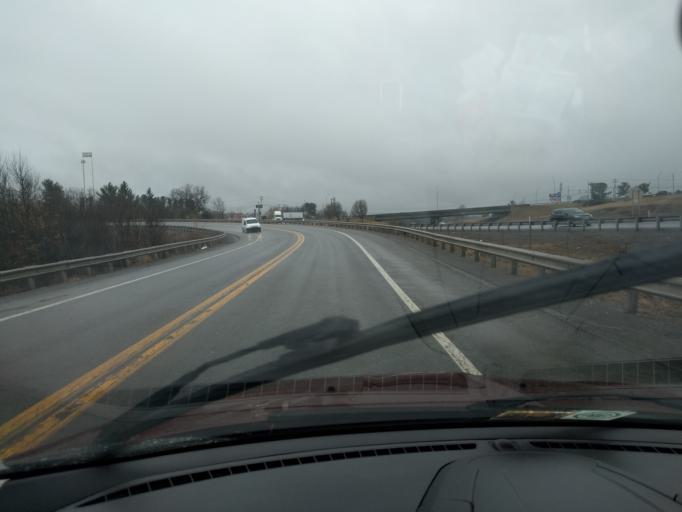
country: US
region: West Virginia
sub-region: Raleigh County
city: Mabscott
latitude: 37.7947
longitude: -81.2144
